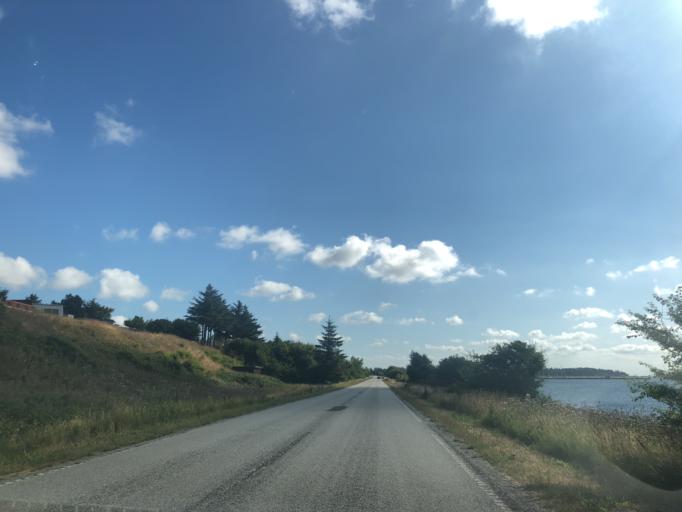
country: DK
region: North Denmark
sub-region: Morso Kommune
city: Nykobing Mors
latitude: 57.0030
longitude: 8.9299
